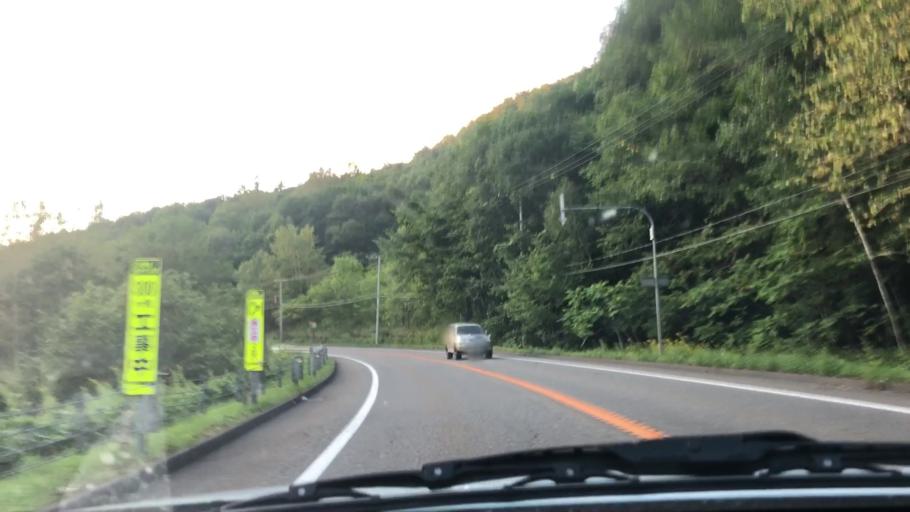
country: JP
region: Hokkaido
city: Shimo-furano
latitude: 42.8911
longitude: 142.2493
